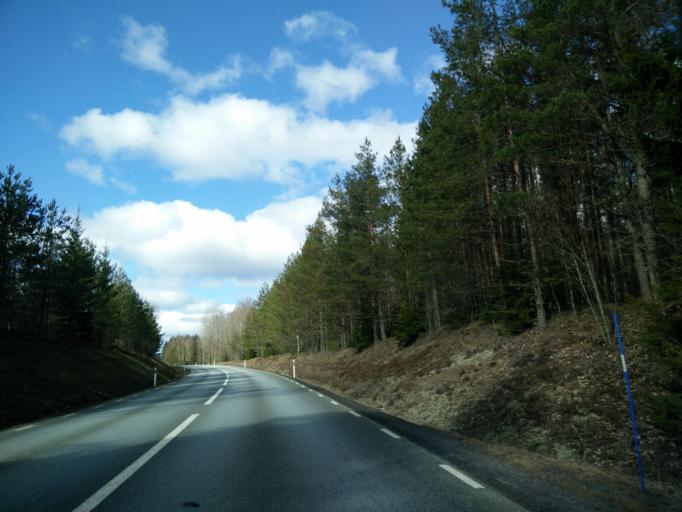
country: SE
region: Vaermland
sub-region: Munkfors Kommun
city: Munkfors
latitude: 59.9552
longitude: 13.5721
